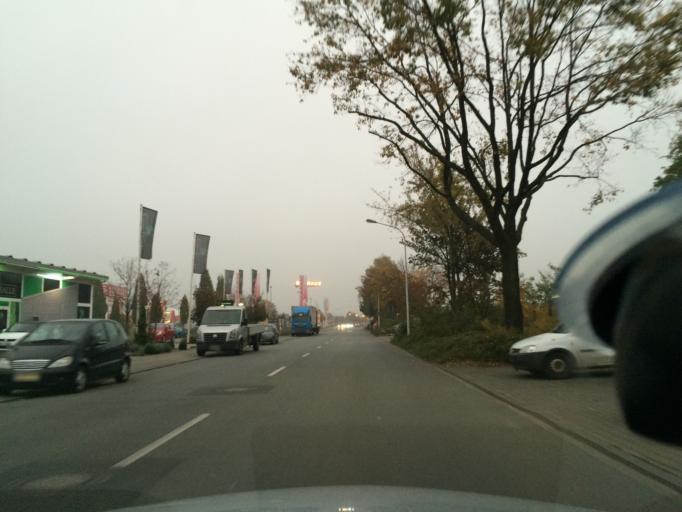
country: DE
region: Hesse
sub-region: Regierungsbezirk Darmstadt
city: Darmstadt
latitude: 49.8856
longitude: 8.6451
